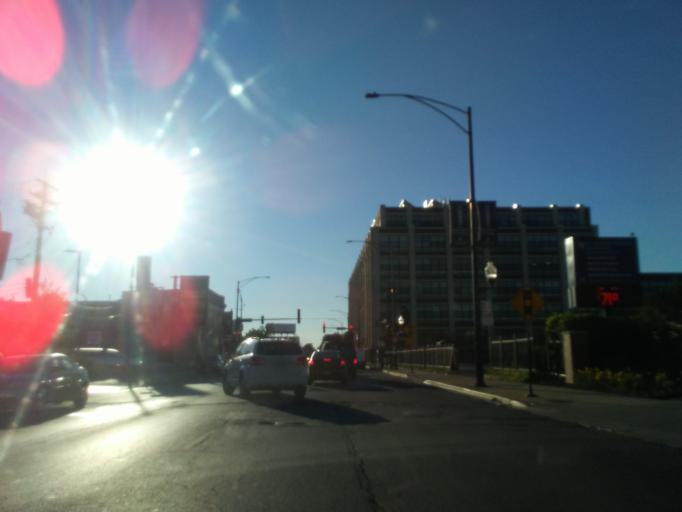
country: US
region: Illinois
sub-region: Cook County
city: Lincolnwood
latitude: 41.9390
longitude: -87.7282
